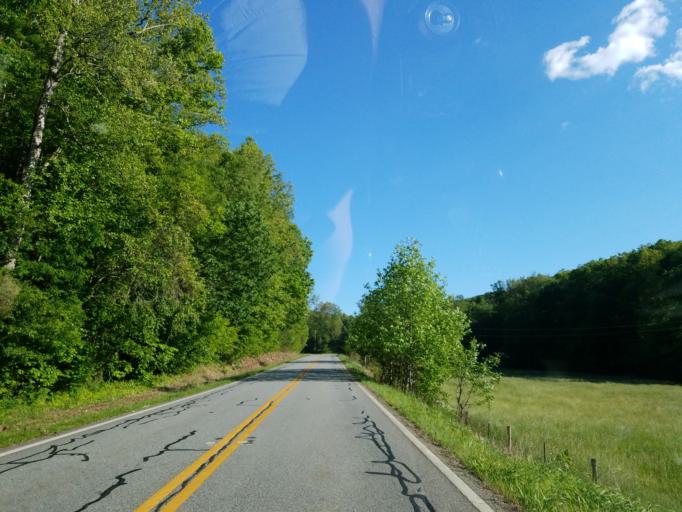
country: US
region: Georgia
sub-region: Fannin County
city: Blue Ridge
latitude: 34.8233
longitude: -84.1890
